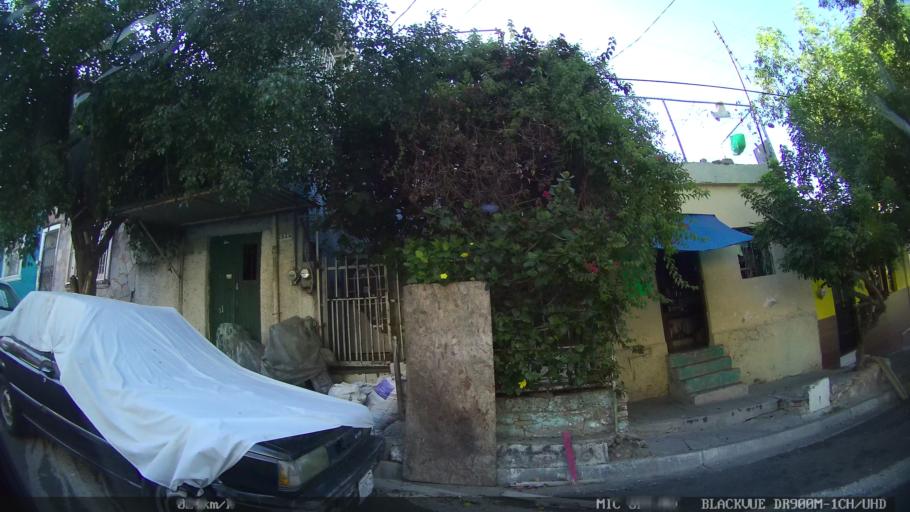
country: MX
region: Jalisco
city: Tlaquepaque
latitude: 20.7081
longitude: -103.2899
